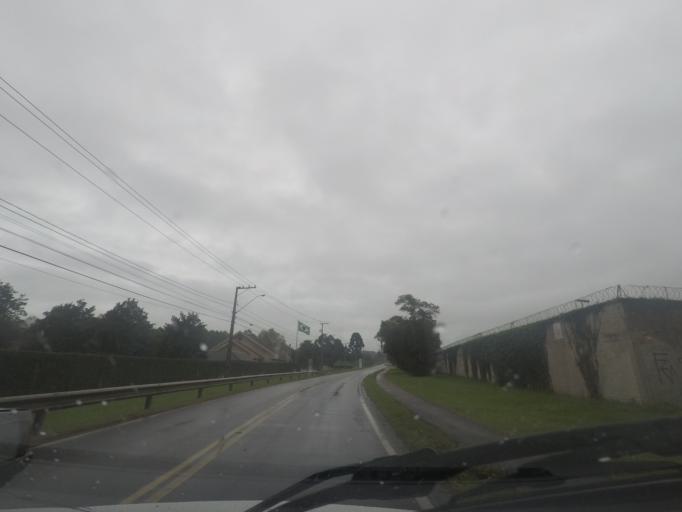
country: BR
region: Parana
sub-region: Quatro Barras
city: Quatro Barras
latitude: -25.3745
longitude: -49.0937
